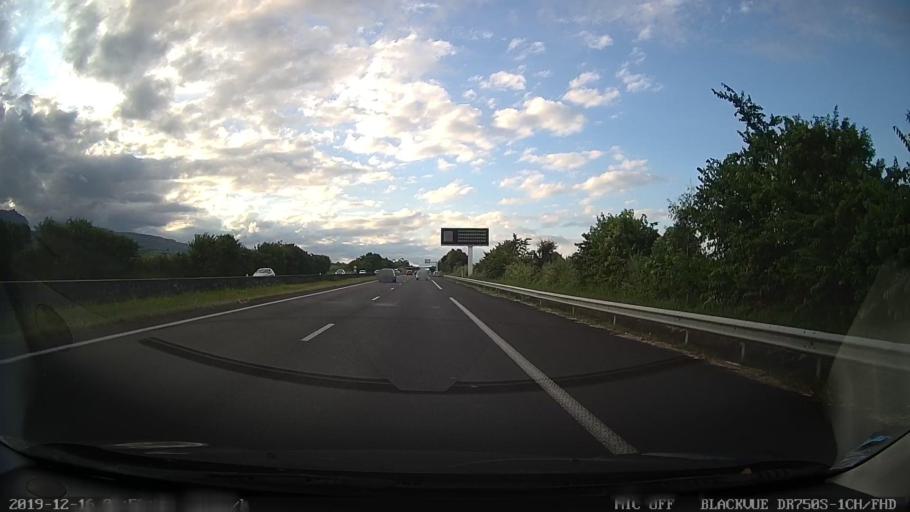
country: RE
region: Reunion
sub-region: Reunion
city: Bras-Panon
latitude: -20.9945
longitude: 55.6679
